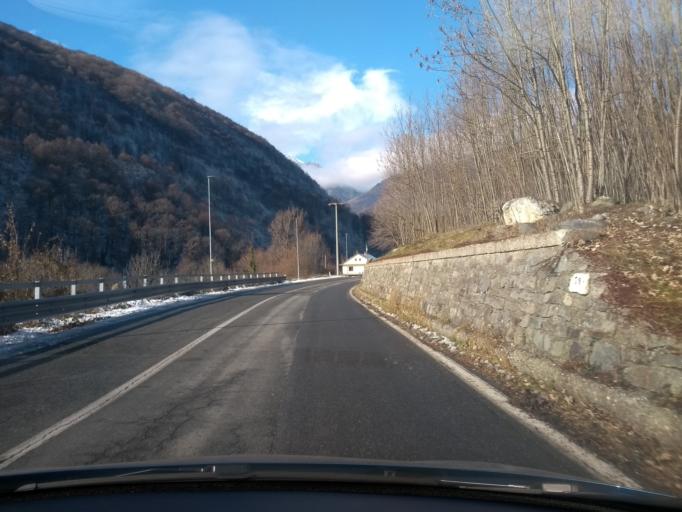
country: IT
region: Piedmont
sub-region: Provincia di Torino
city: Mezzenile
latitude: 45.3048
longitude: 7.3961
